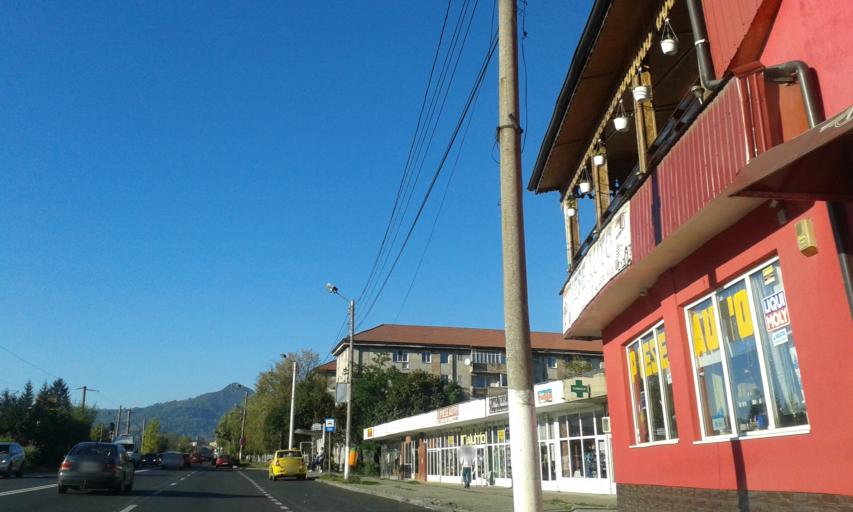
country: RO
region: Hunedoara
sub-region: Municipiul Petrosani
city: Petrosani
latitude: 45.4024
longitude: 23.3729
